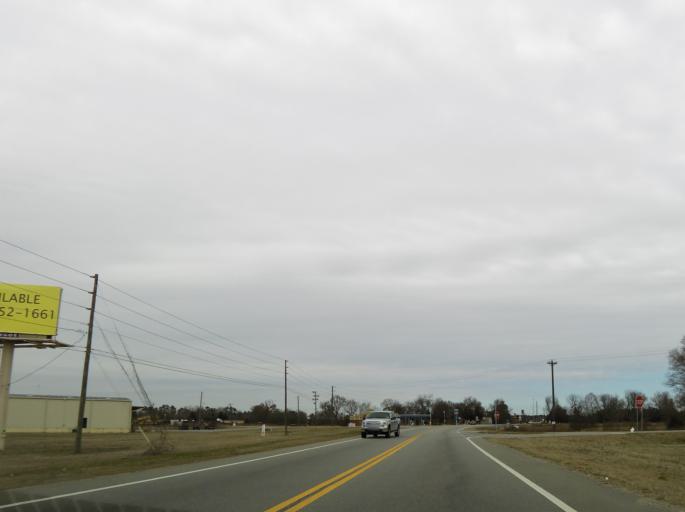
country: US
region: Georgia
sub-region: Peach County
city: Byron
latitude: 32.6085
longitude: -83.7487
